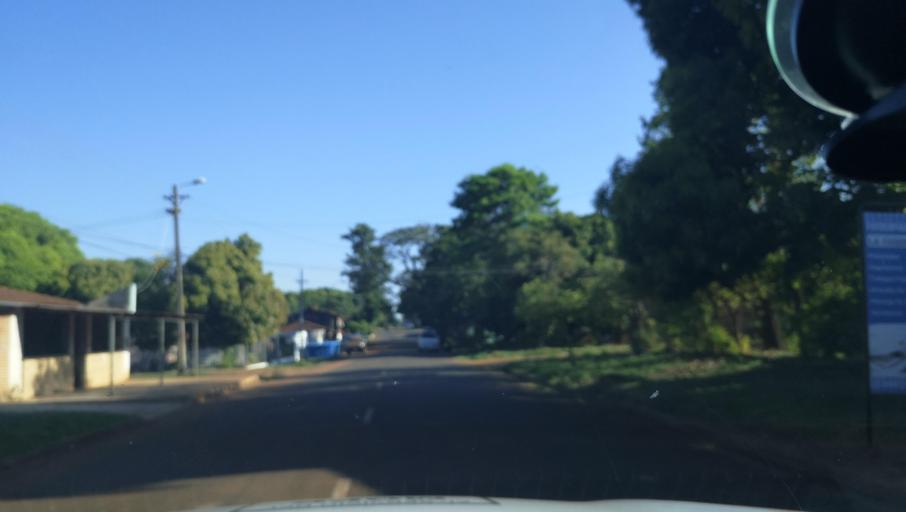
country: PY
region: Itapua
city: Carmen del Parana
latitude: -27.1651
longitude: -56.2431
